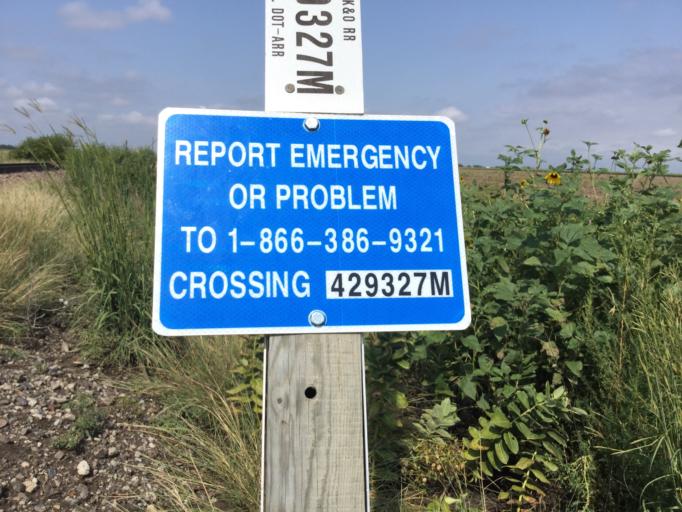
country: US
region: Kansas
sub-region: Rush County
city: La Crosse
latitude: 38.5434
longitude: -99.3469
